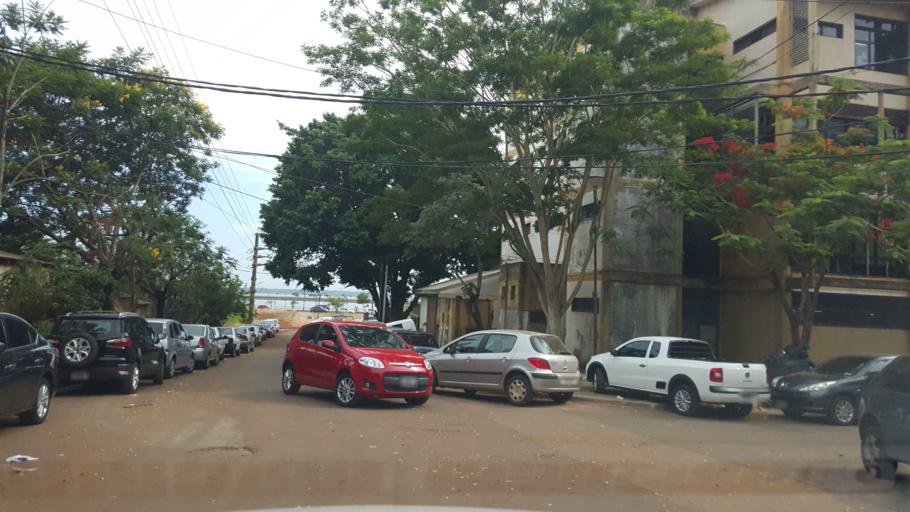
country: AR
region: Misiones
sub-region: Departamento de Capital
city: Posadas
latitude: -27.3579
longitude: -55.9057
